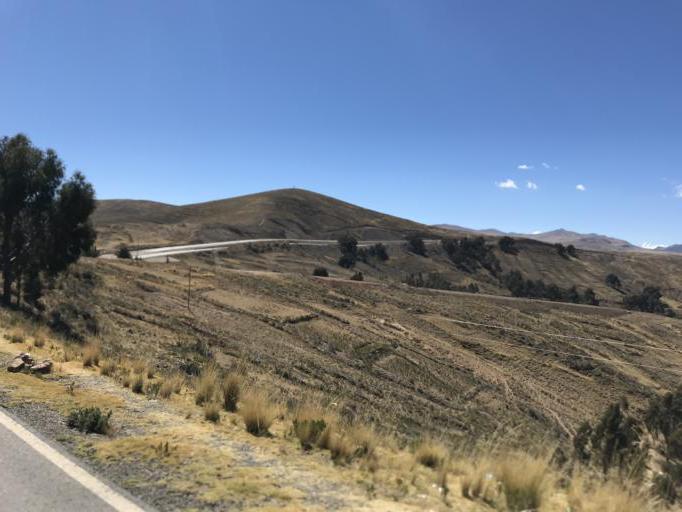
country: BO
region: La Paz
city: San Pablo
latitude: -16.2059
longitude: -68.8325
